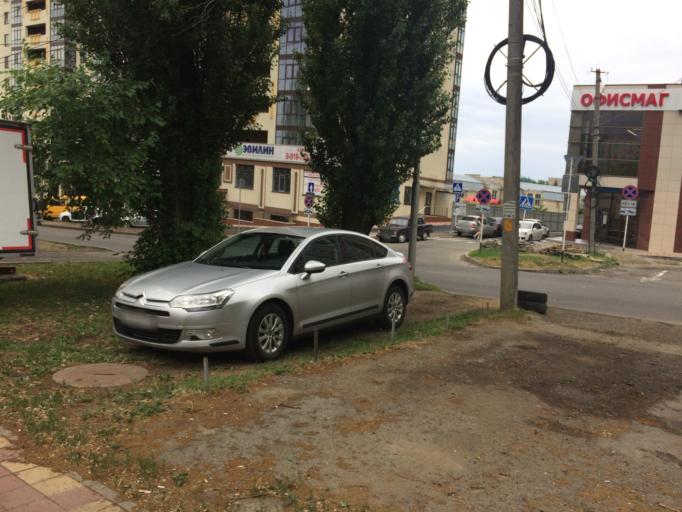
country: RU
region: Stavropol'skiy
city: Stavropol'
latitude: 45.0408
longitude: 41.9798
